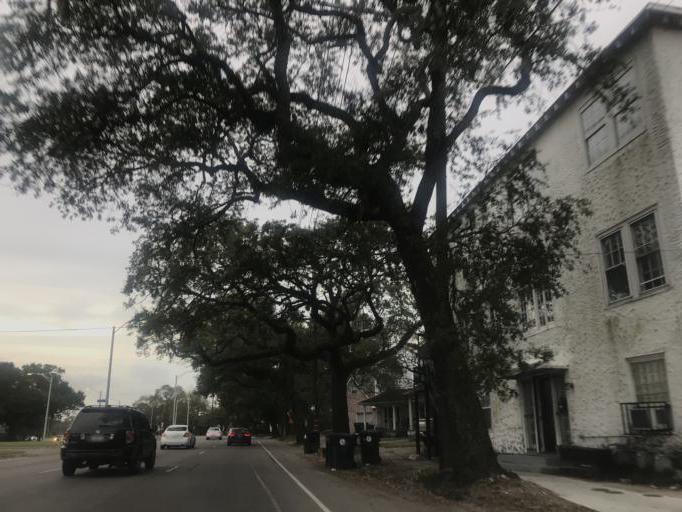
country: US
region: Louisiana
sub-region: Jefferson Parish
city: Jefferson
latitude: 29.9516
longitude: -90.1160
